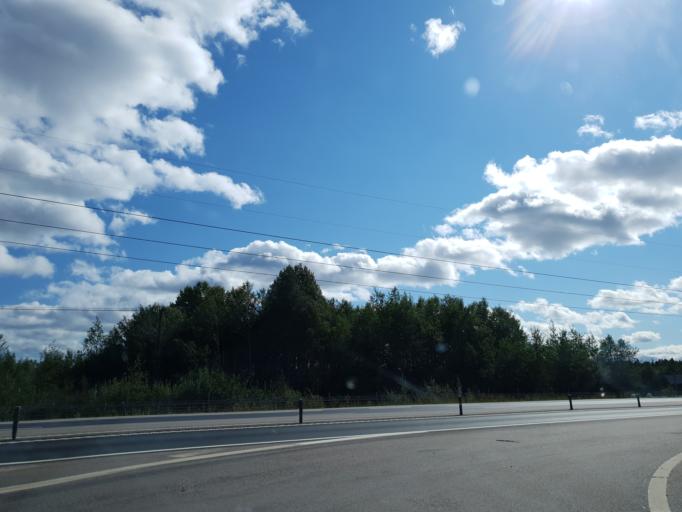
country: SE
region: Vaesterbotten
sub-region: Nordmalings Kommun
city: Nordmaling
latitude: 63.5346
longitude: 19.3996
